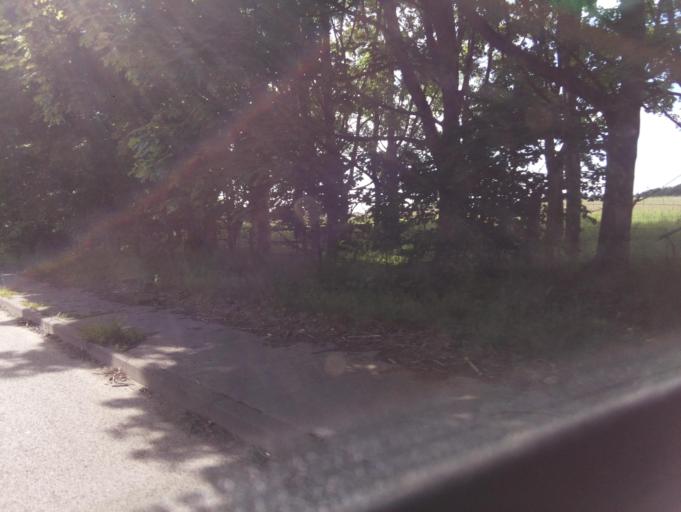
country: GB
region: England
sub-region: Hertfordshire
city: Kings Langley
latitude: 51.6764
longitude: -0.4464
